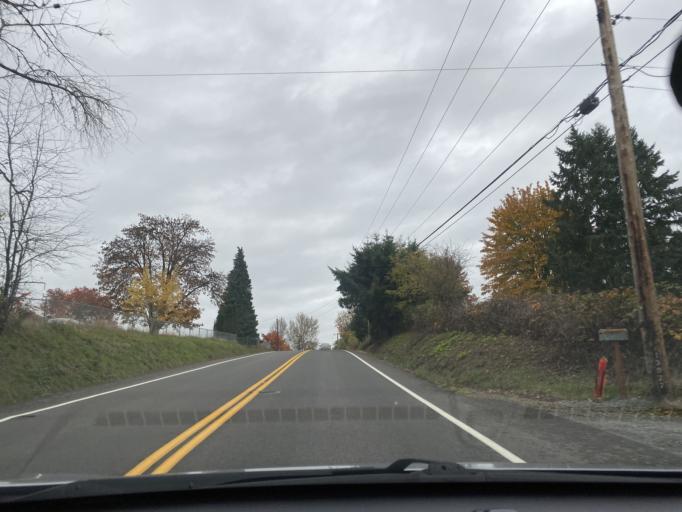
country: US
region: Washington
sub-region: King County
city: Lea Hill
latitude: 47.3008
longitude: -122.1551
